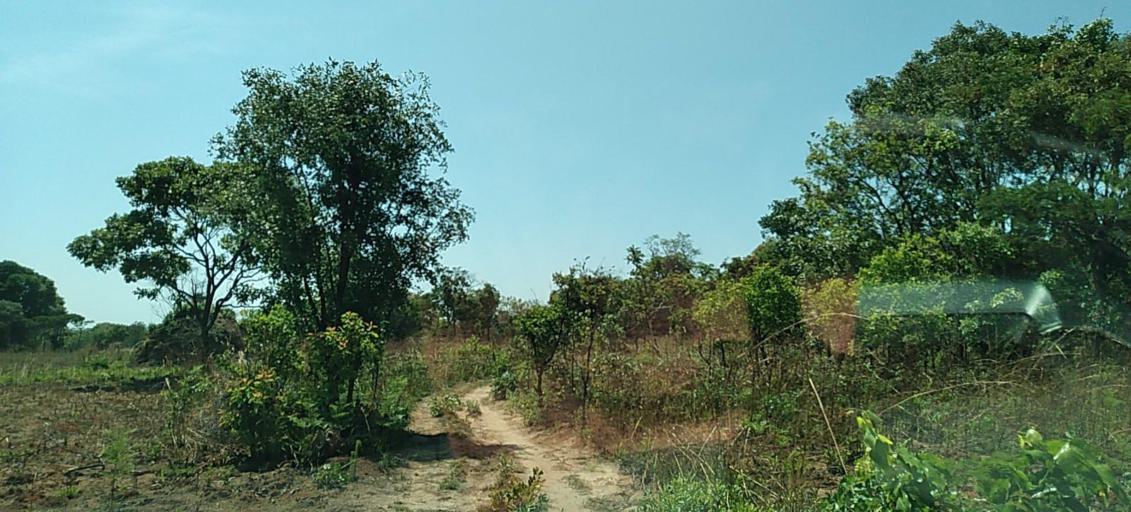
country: ZM
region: Copperbelt
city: Chililabombwe
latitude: -12.2902
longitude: 27.8929
